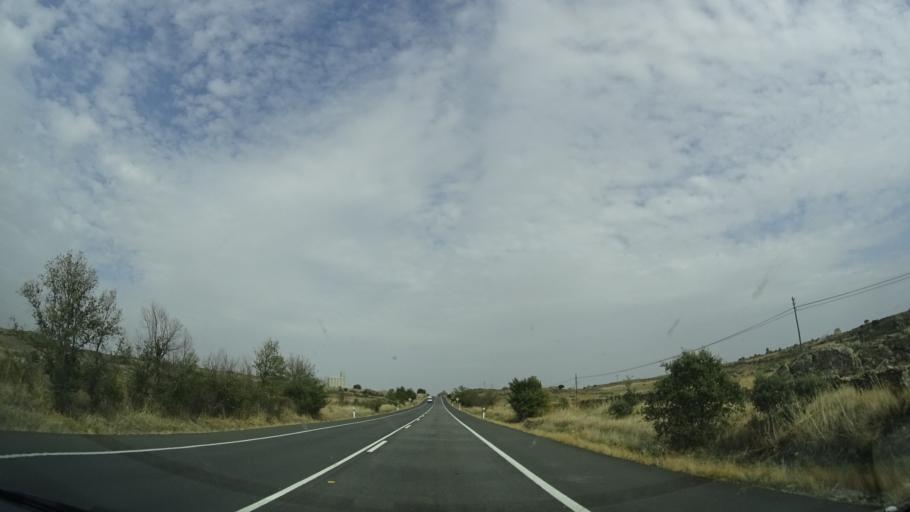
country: ES
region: Extremadura
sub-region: Provincia de Caceres
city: Trujillo
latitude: 39.4431
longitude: -5.8848
